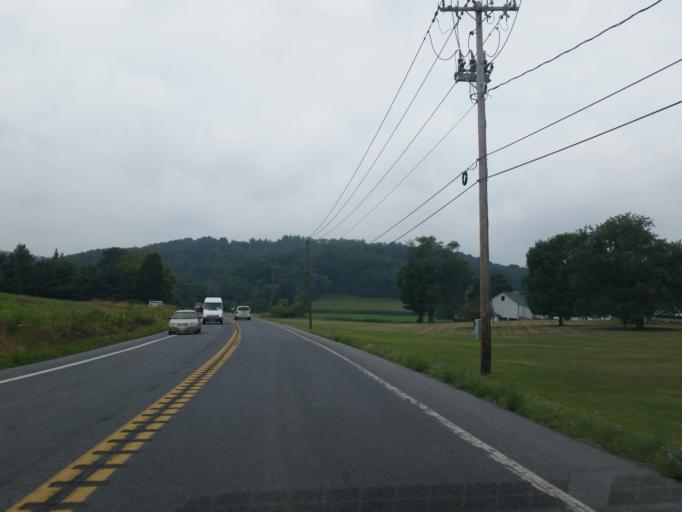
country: US
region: Pennsylvania
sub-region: Lancaster County
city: Brickerville
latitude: 40.2702
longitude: -76.3020
